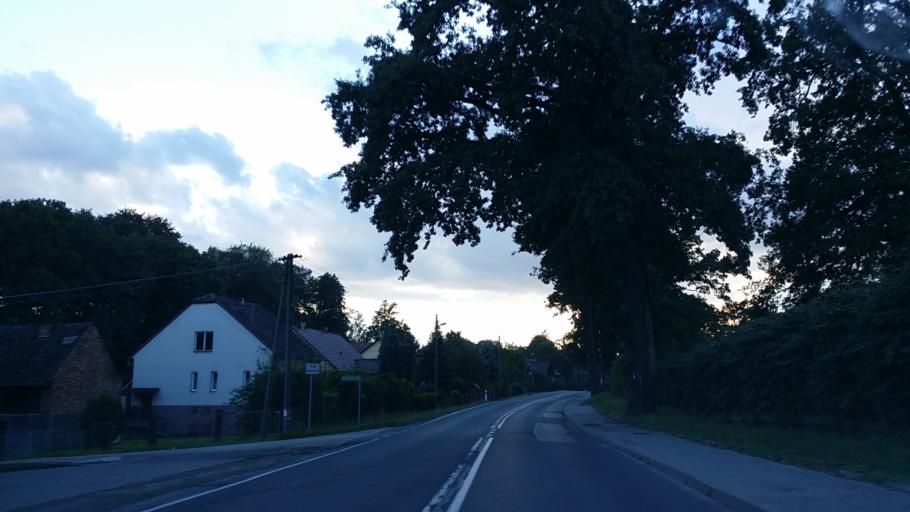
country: PL
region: Lesser Poland Voivodeship
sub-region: Powiat oswiecimski
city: Polanka Wielka
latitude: 49.9850
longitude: 19.3231
